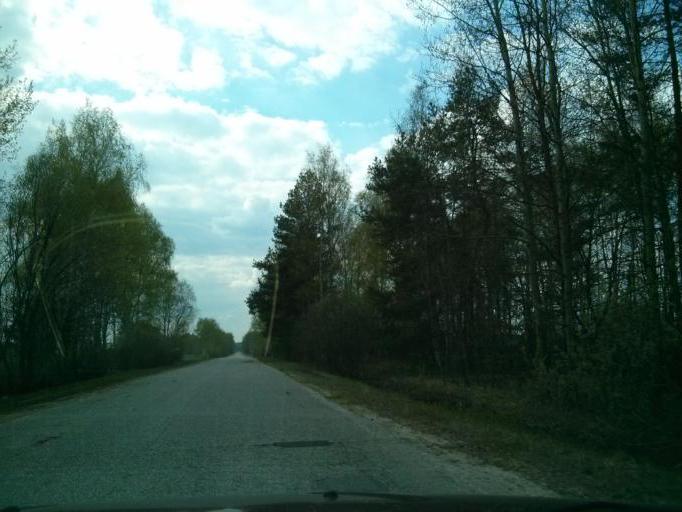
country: RU
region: Nizjnij Novgorod
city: Shimorskoye
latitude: 55.3413
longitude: 41.8367
